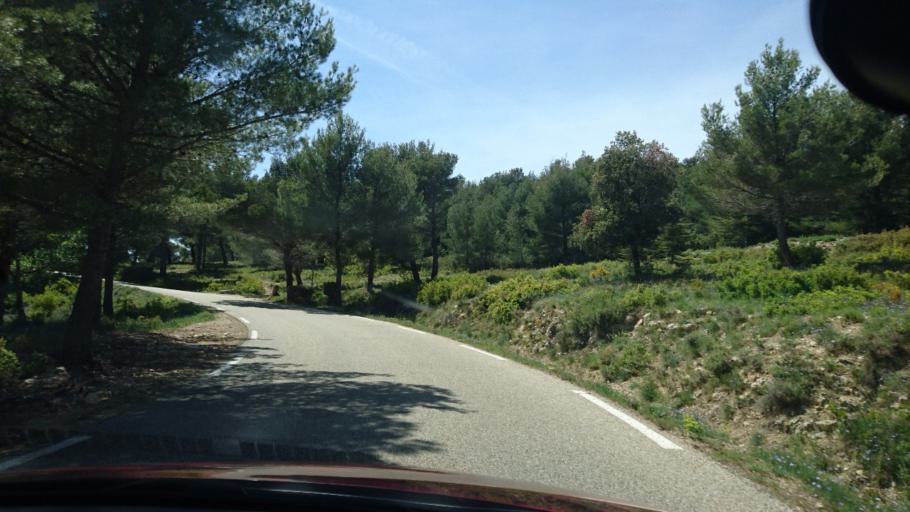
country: FR
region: Provence-Alpes-Cote d'Azur
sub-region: Departement du Vaucluse
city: Malaucene
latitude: 44.1410
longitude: 5.1339
